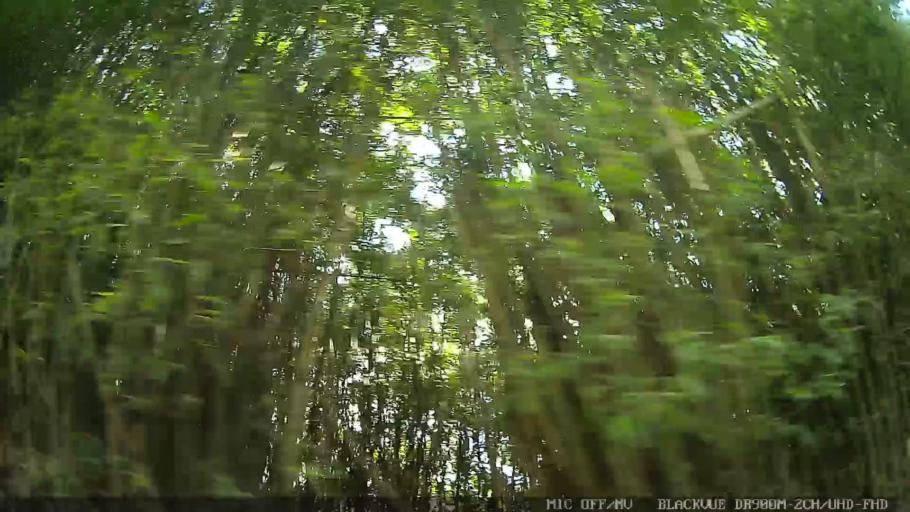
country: BR
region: Sao Paulo
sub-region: Braganca Paulista
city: Braganca Paulista
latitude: -22.9749
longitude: -46.5067
